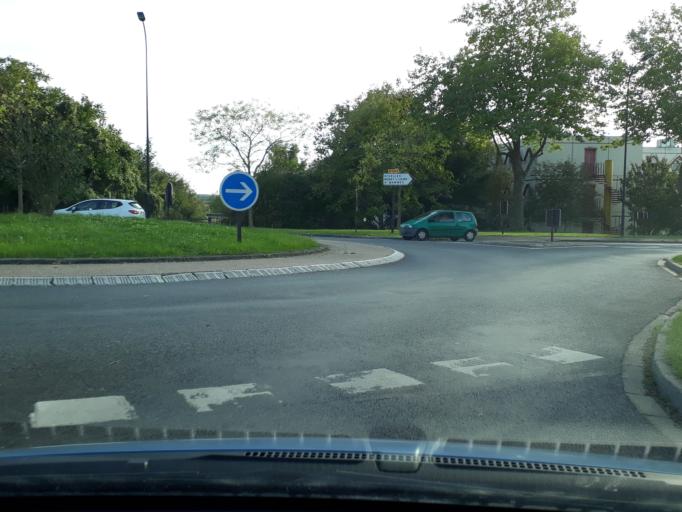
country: FR
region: Ile-de-France
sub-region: Departement de Seine-et-Marne
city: Ecuelles
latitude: 48.3680
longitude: 2.8399
